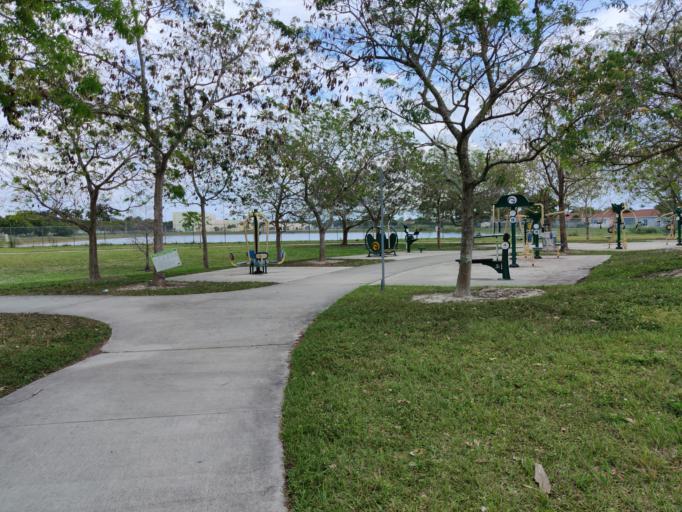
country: US
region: Florida
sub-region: Miami-Dade County
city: Kendall West
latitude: 25.7195
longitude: -80.4540
